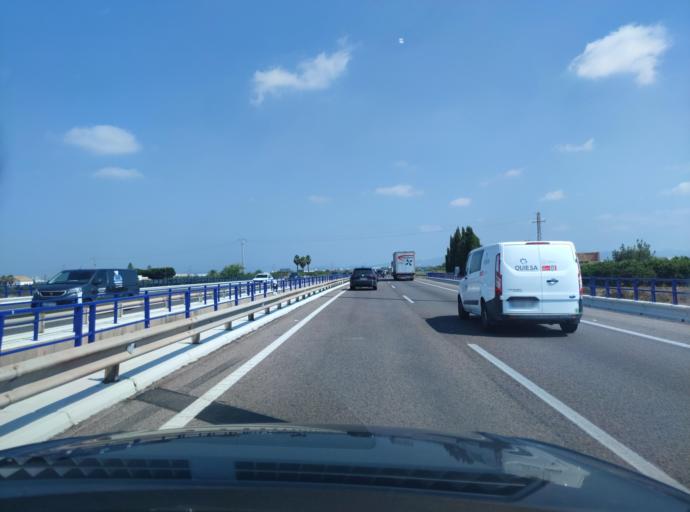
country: ES
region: Valencia
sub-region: Provincia de Castello
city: Alquerias del Nino Perdido
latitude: 39.9098
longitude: -0.1352
